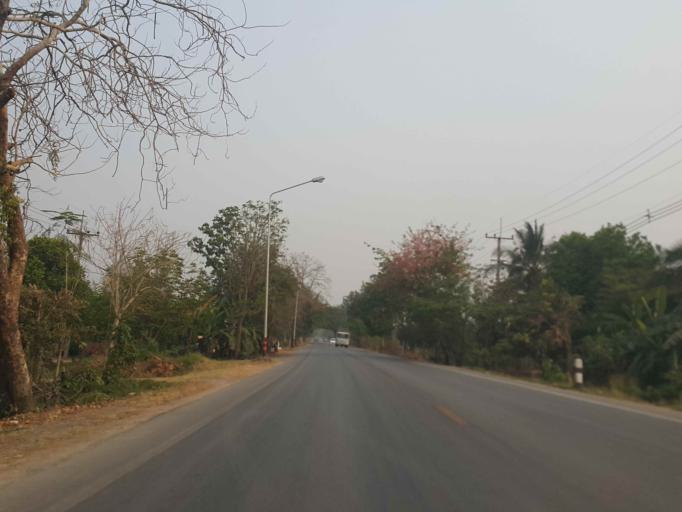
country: TH
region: Chiang Mai
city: Mae Taeng
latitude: 19.0502
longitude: 98.9622
